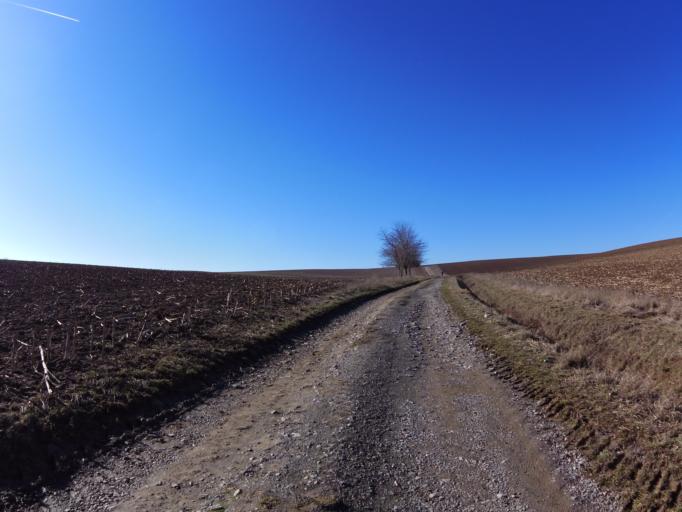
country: DE
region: Bavaria
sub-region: Regierungsbezirk Unterfranken
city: Estenfeld
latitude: 49.8453
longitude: 9.9964
